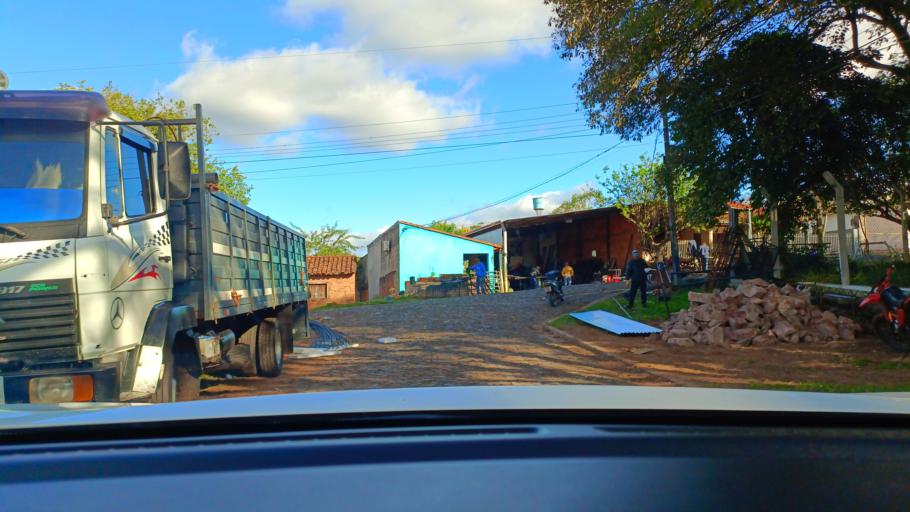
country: PY
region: San Pedro
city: Guayaybi
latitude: -24.6736
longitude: -56.4394
